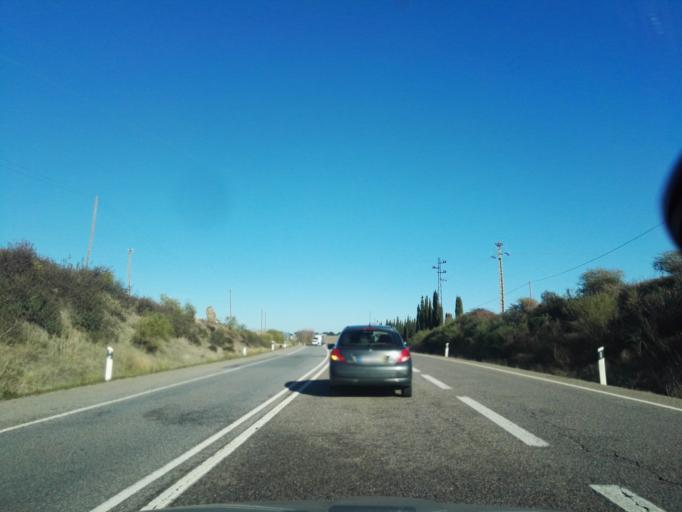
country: PT
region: Evora
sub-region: Borba
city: Borba
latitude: 38.8227
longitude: -7.4252
